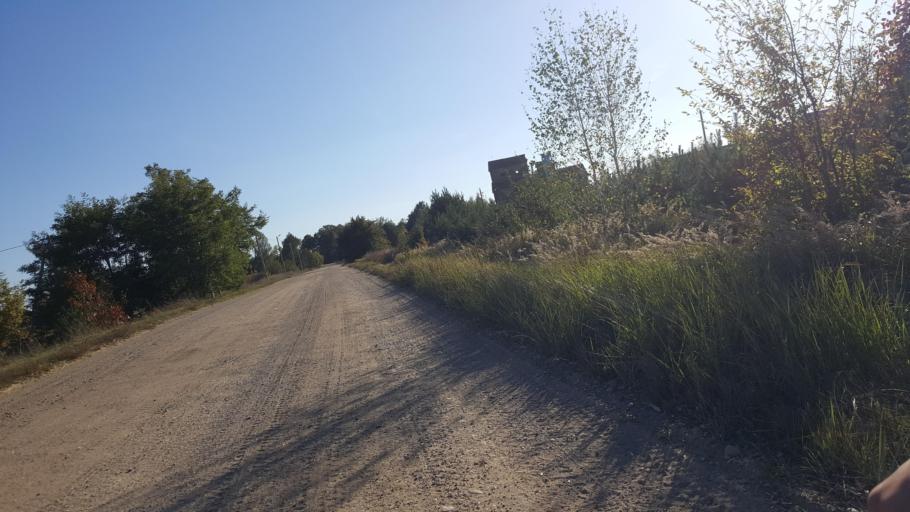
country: BY
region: Brest
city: Kamyanyets
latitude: 52.3964
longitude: 23.8853
